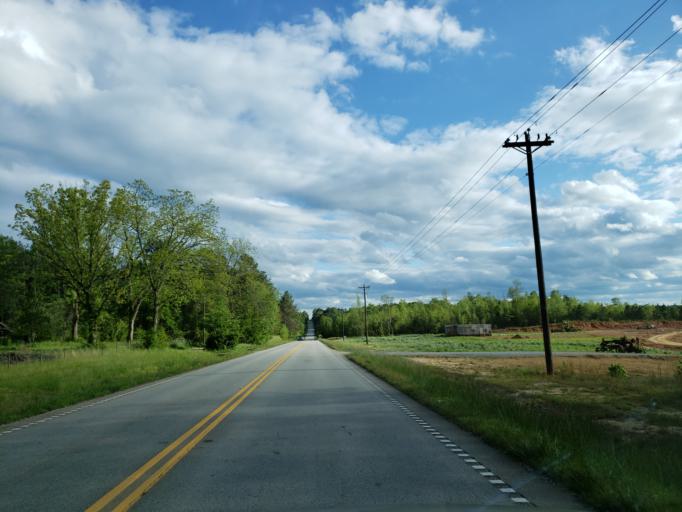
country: US
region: Georgia
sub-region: Haralson County
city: Tallapoosa
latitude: 33.8216
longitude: -85.2916
